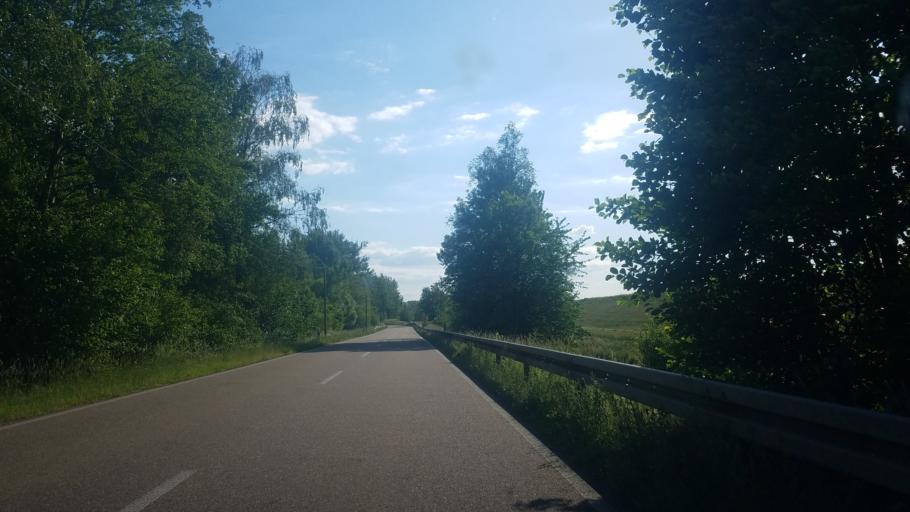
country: FR
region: Alsace
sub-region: Departement du Bas-Rhin
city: Kilstett
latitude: 48.6503
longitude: 7.8659
